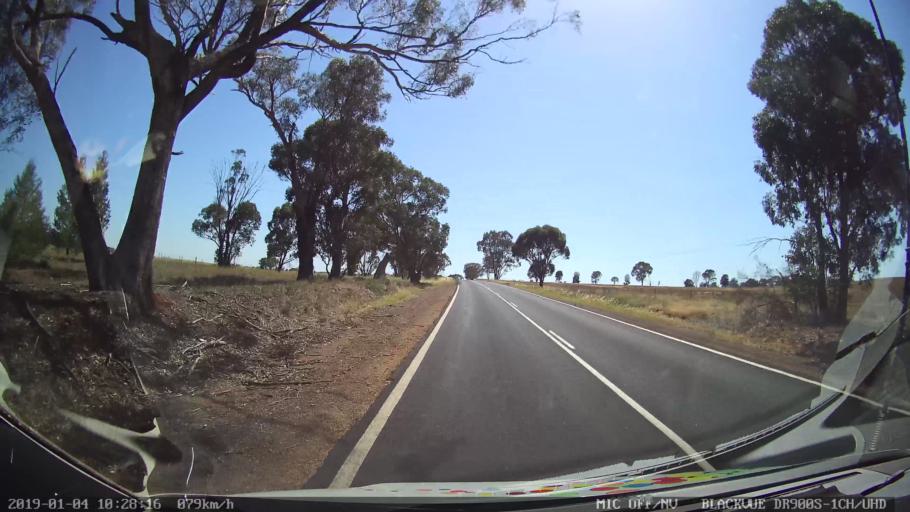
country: AU
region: New South Wales
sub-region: Cabonne
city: Canowindra
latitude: -33.3643
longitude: 148.6077
